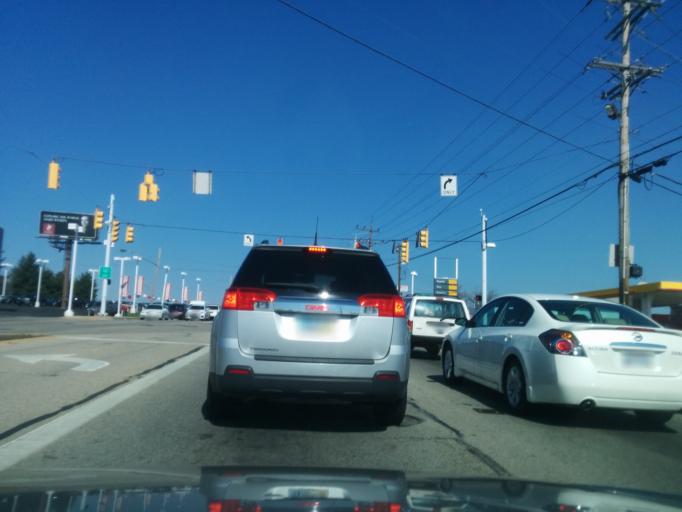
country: US
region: Ohio
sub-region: Hamilton County
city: Northbrook
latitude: 39.2366
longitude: -84.5922
